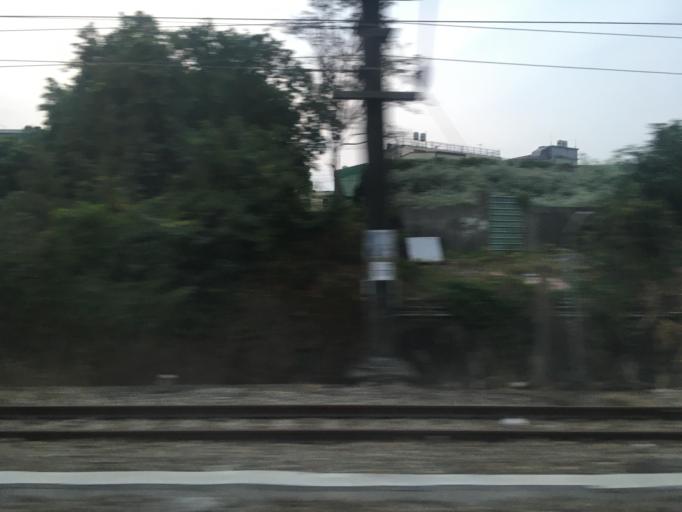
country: TW
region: Taiwan
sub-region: Pingtung
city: Pingtung
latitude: 22.6588
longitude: 120.4218
